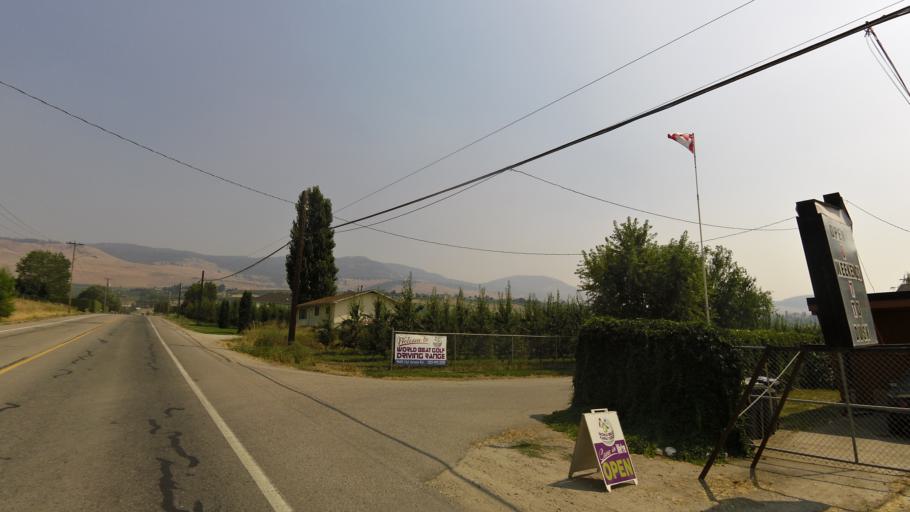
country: CA
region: British Columbia
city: Kelowna
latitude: 49.9181
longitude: -119.3751
